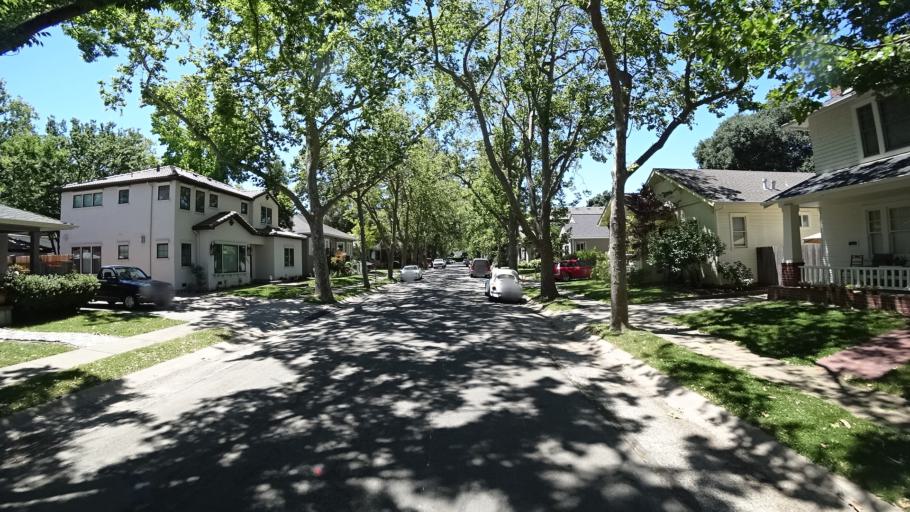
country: US
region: California
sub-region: Sacramento County
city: Sacramento
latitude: 38.5700
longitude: -121.4485
